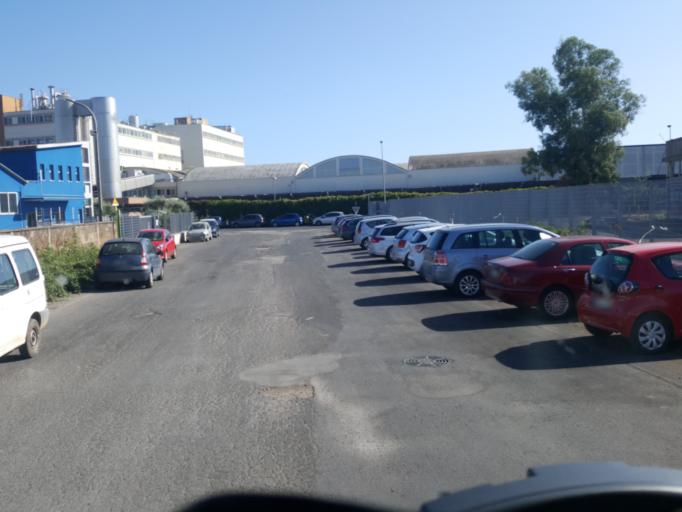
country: IT
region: Latium
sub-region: Citta metropolitana di Roma Capitale
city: Anzio
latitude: 41.5143
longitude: 12.6256
